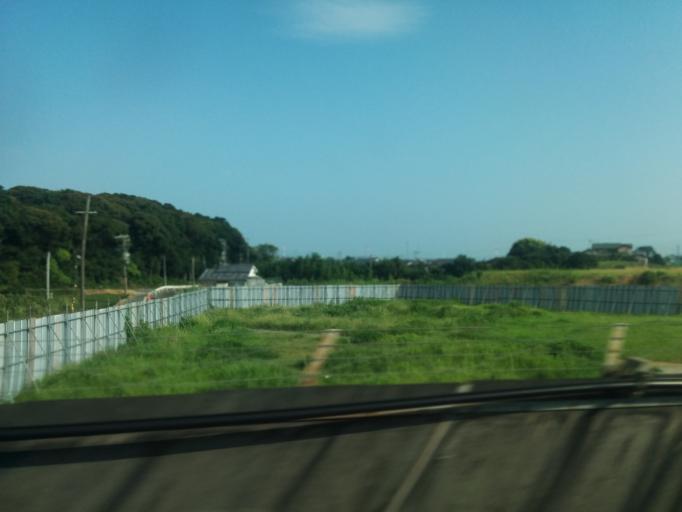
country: JP
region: Shizuoka
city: Iwata
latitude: 34.7185
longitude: 137.8861
